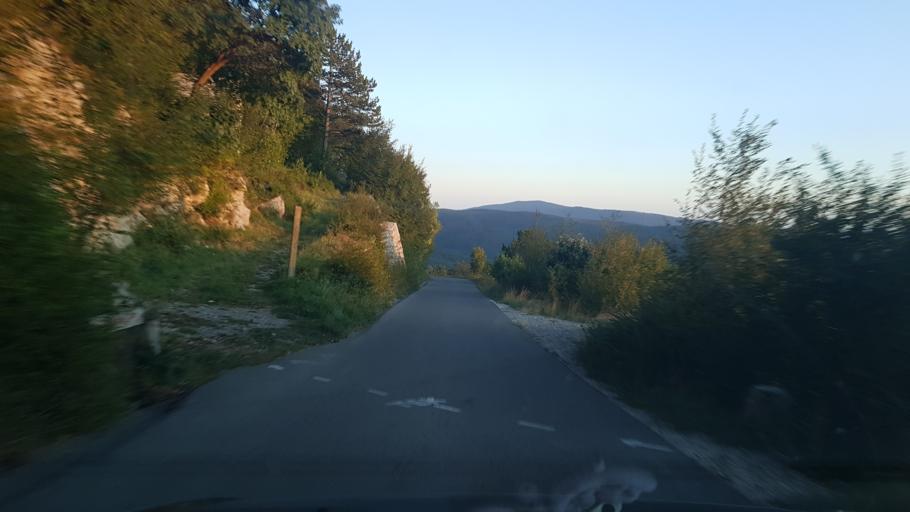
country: SI
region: Vipava
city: Vipava
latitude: 45.7938
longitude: 14.0090
